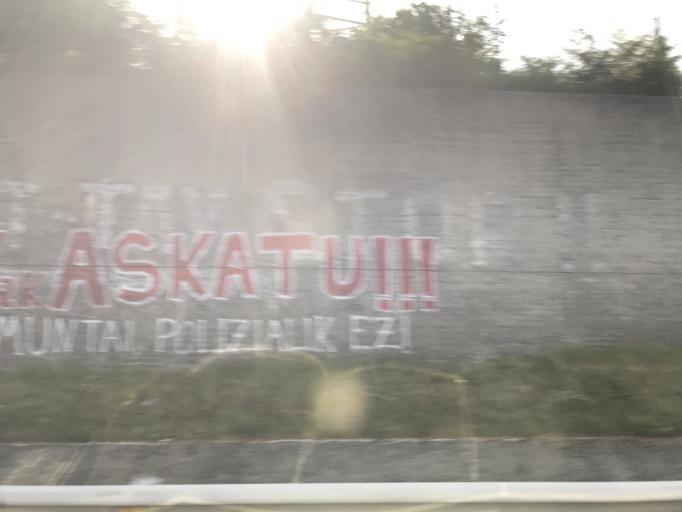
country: ES
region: Navarre
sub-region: Provincia de Navarra
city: Altsasu
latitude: 42.9017
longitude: -2.1754
